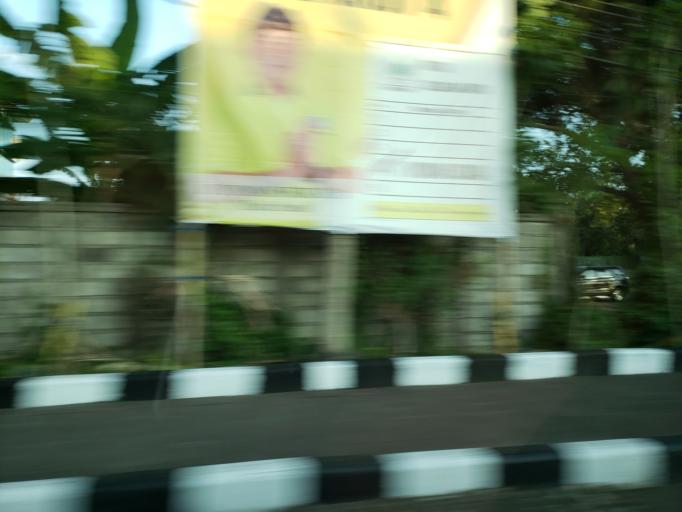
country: ID
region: Bali
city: Kelanabian
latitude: -8.7659
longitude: 115.1785
